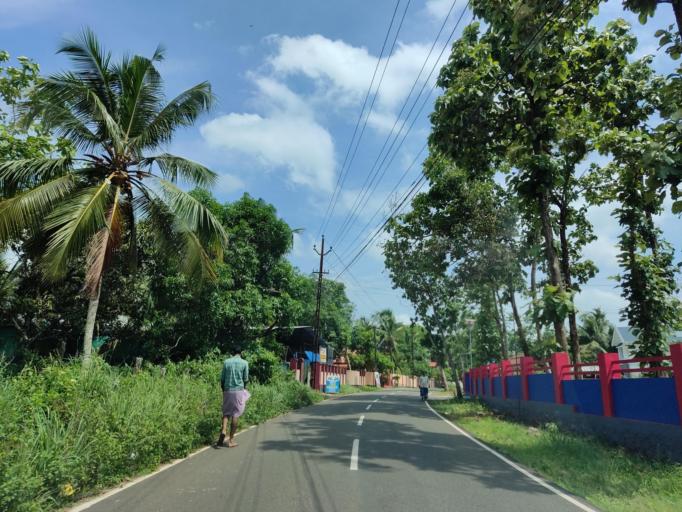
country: IN
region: Kerala
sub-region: Alappuzha
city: Mavelikara
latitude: 9.2790
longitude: 76.5680
